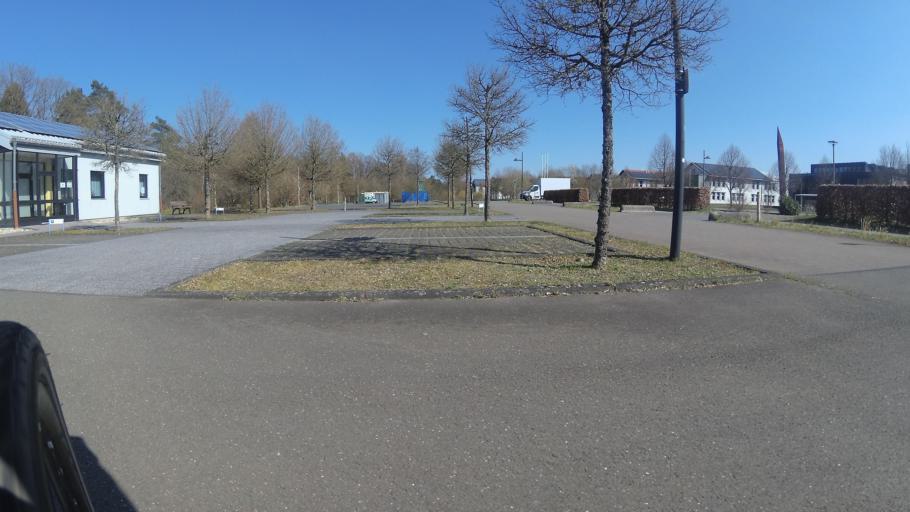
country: DE
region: Rheinland-Pfalz
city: Ellweiler
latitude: 49.6094
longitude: 7.1678
